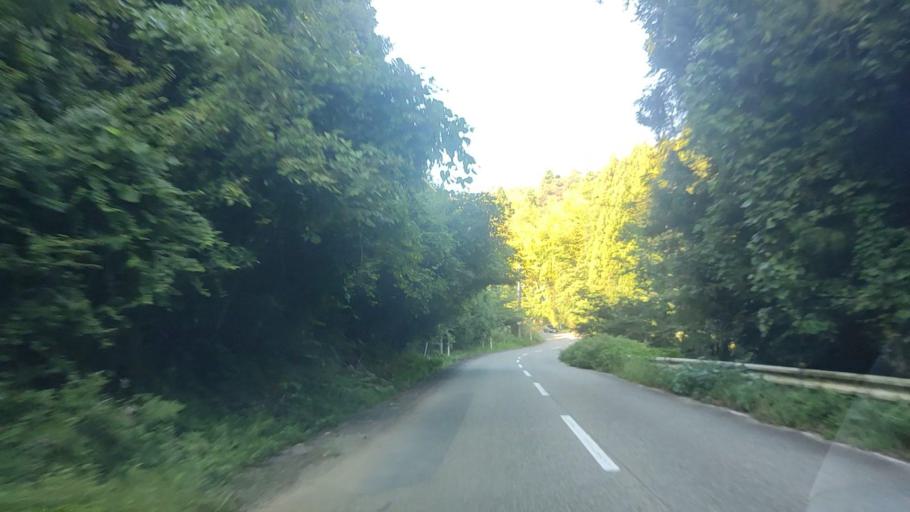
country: JP
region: Ishikawa
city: Nanao
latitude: 37.1140
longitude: 136.9651
